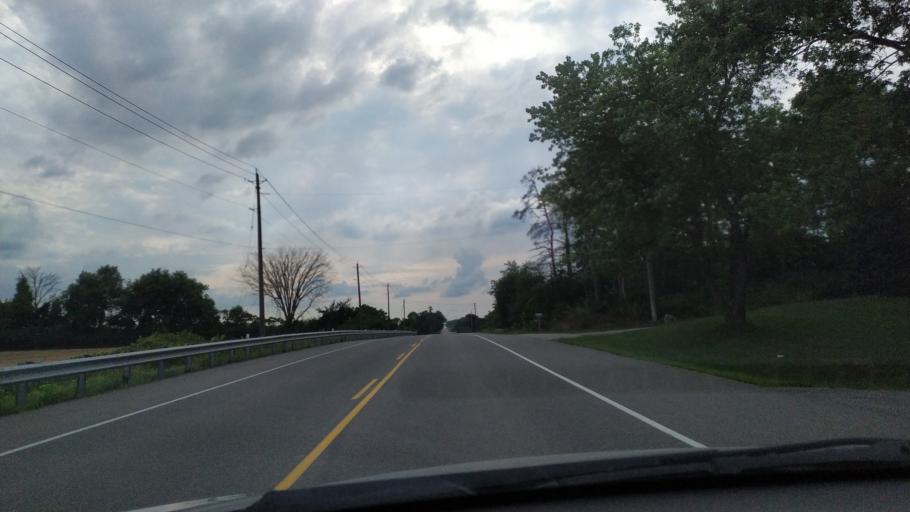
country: CA
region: Ontario
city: Kitchener
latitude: 43.3606
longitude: -80.4672
